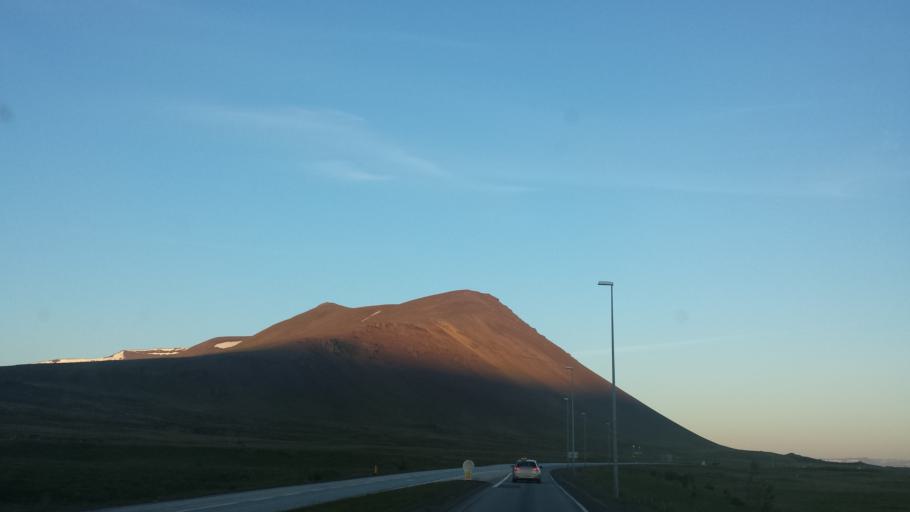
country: IS
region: Capital Region
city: Reykjavik
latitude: 64.2741
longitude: -21.8384
